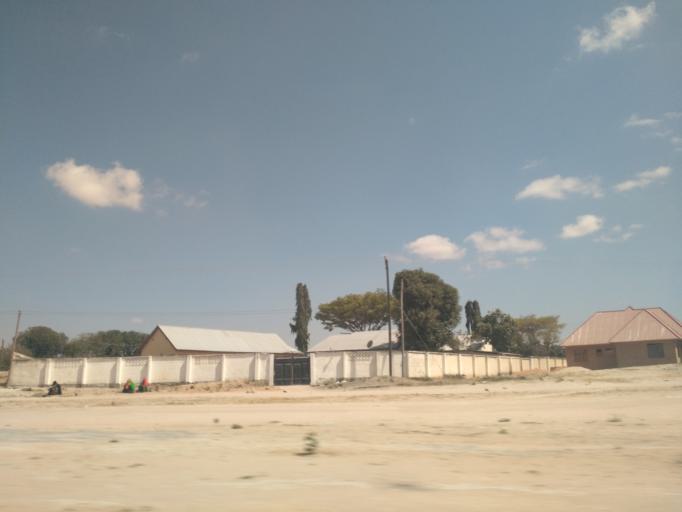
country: TZ
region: Dodoma
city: Dodoma
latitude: -6.1495
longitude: 35.7298
